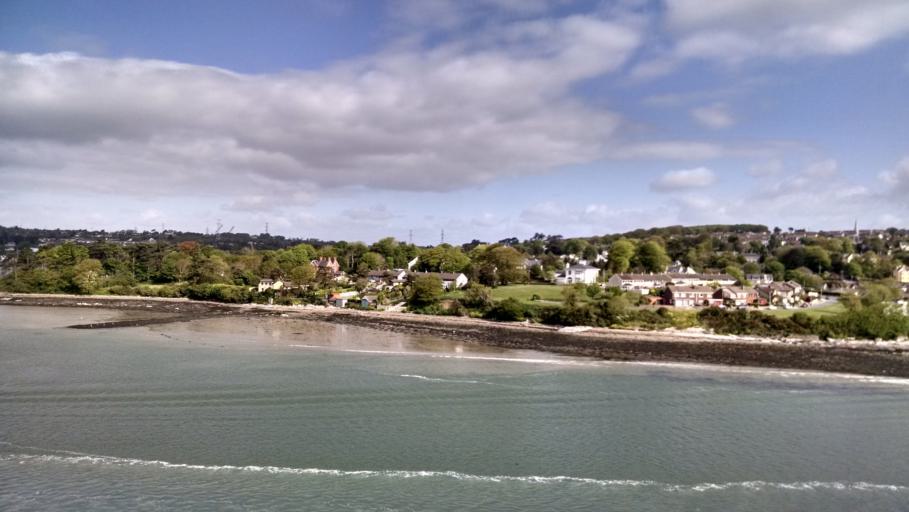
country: IE
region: Munster
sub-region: County Cork
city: Cobh
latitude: 51.8411
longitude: -8.3127
